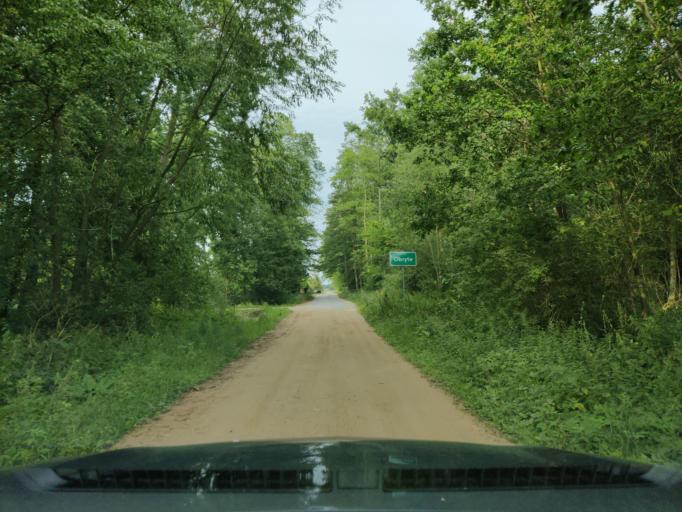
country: PL
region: Masovian Voivodeship
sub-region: Powiat pultuski
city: Obryte
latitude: 52.7052
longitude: 21.2258
